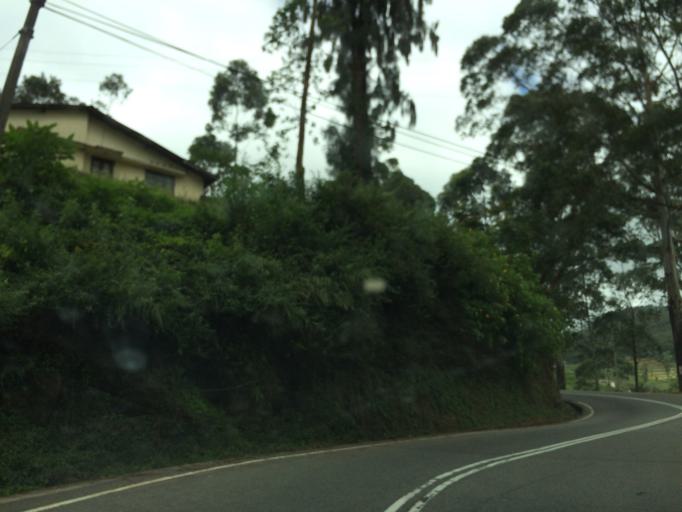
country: LK
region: Central
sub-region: Nuwara Eliya District
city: Nuwara Eliya
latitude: 7.0246
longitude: 80.7207
